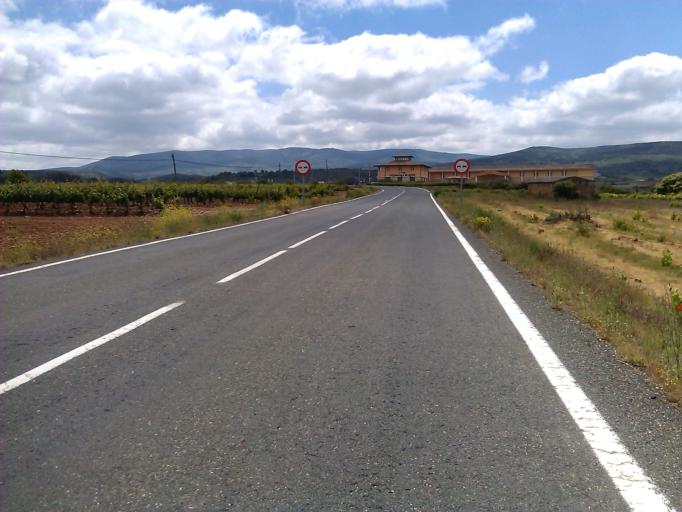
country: ES
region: La Rioja
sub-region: Provincia de La Rioja
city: Hornos de Moncalvillo
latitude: 42.4167
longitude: -2.5922
